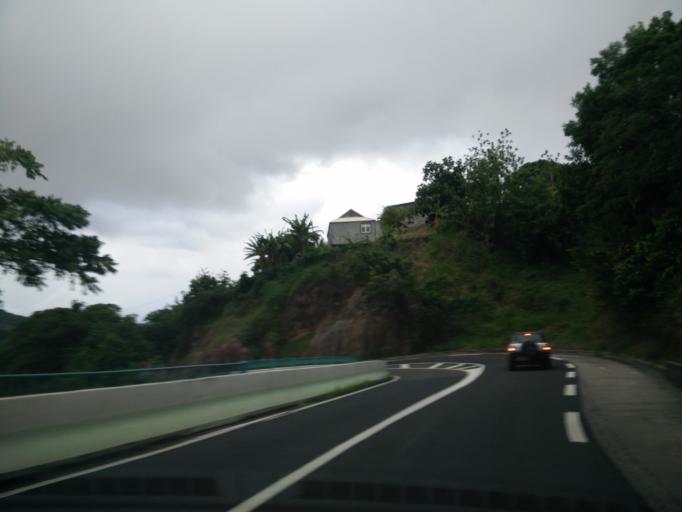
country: MQ
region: Martinique
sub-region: Martinique
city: Le Marin
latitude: 14.4943
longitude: -60.8582
